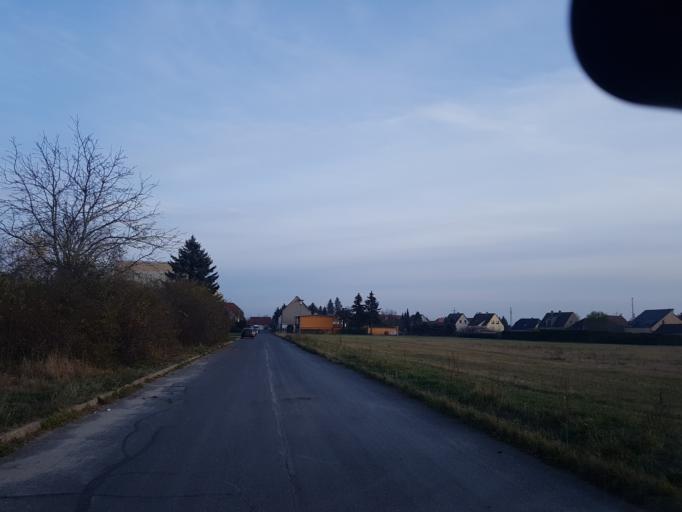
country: DE
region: Brandenburg
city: Finsterwalde
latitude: 51.6434
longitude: 13.7265
